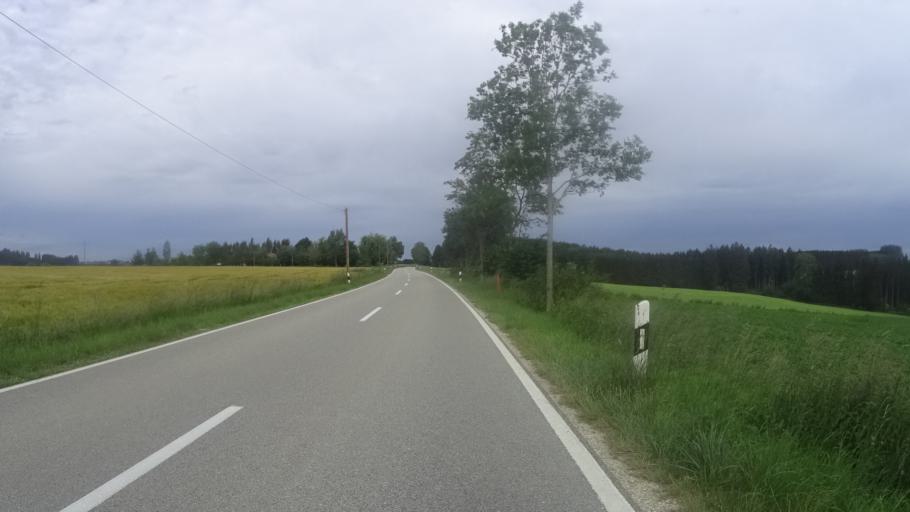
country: DE
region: Bavaria
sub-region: Upper Bavaria
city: Lengdorf
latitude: 48.3053
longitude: 12.0351
